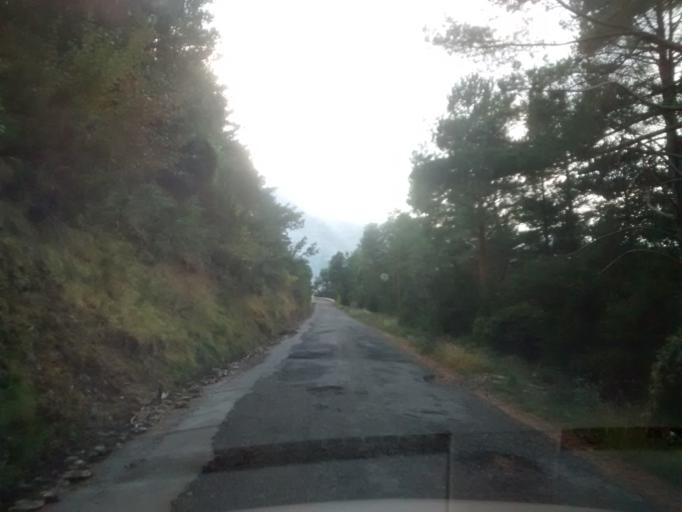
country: ES
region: Aragon
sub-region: Provincia de Huesca
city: Puertolas
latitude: 42.5877
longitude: 0.1674
